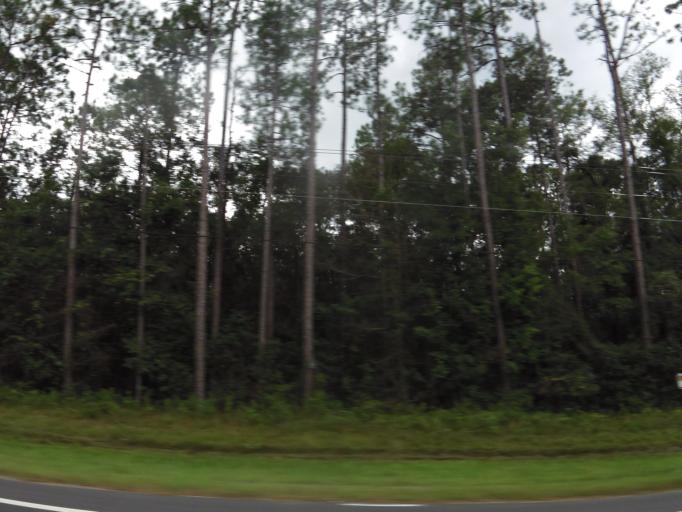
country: US
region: Florida
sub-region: Clay County
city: Middleburg
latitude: 30.0521
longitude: -81.8599
